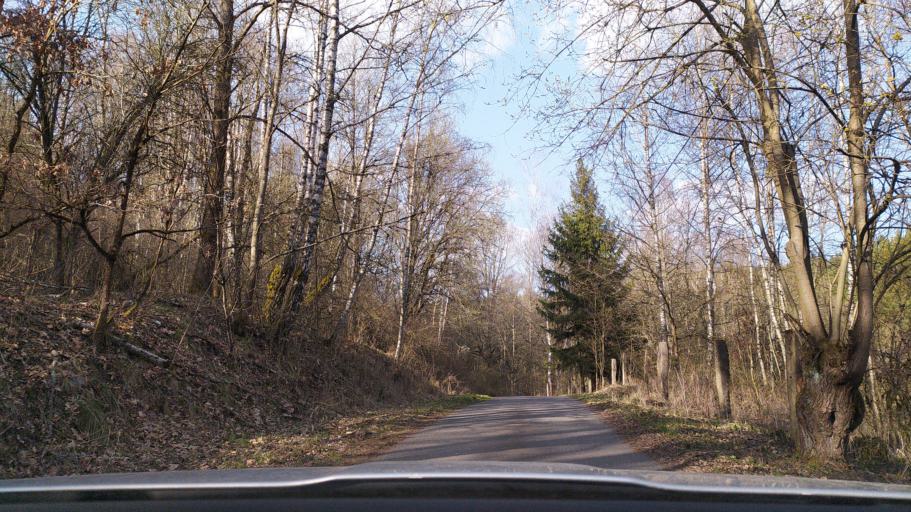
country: DE
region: Bavaria
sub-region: Upper Franconia
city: Hohenberg an der Eger
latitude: 50.1143
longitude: 12.2279
